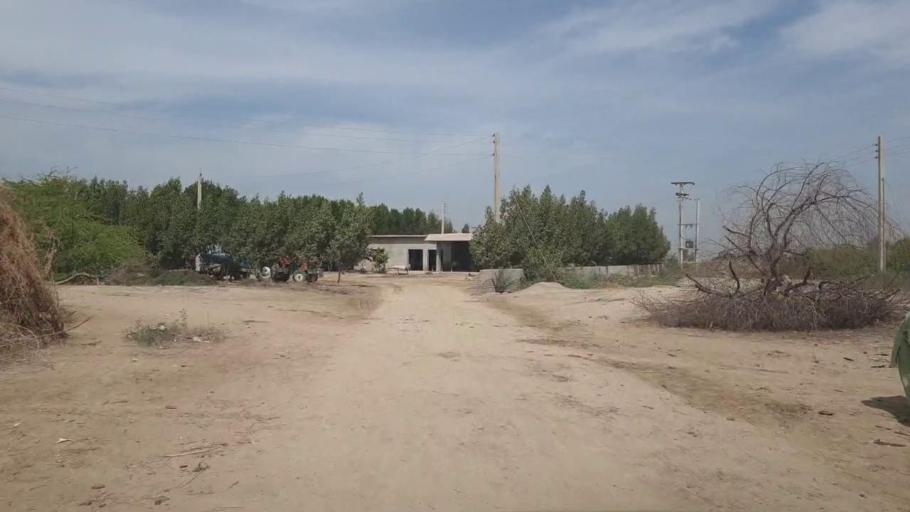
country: PK
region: Sindh
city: Kunri
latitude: 25.2253
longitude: 69.6575
